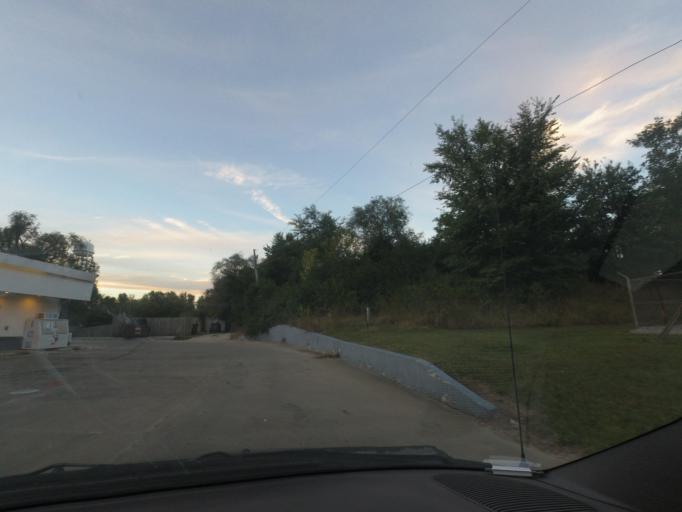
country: US
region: Illinois
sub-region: Pike County
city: Barry
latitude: 39.7009
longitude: -91.0417
